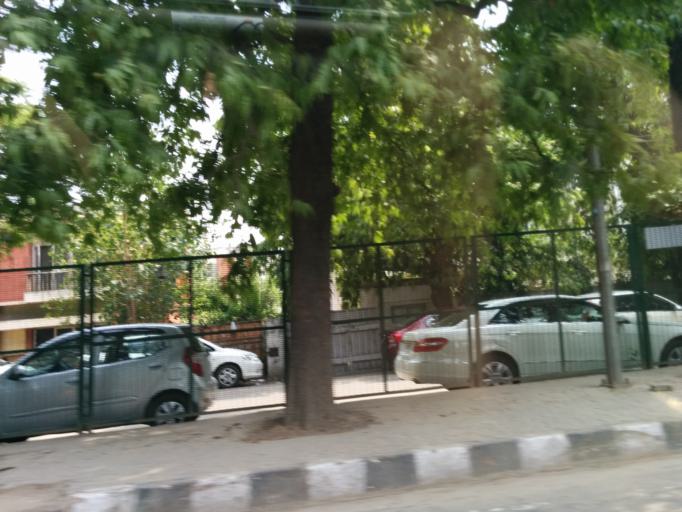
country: IN
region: NCT
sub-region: New Delhi
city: New Delhi
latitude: 28.5431
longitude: 77.2147
